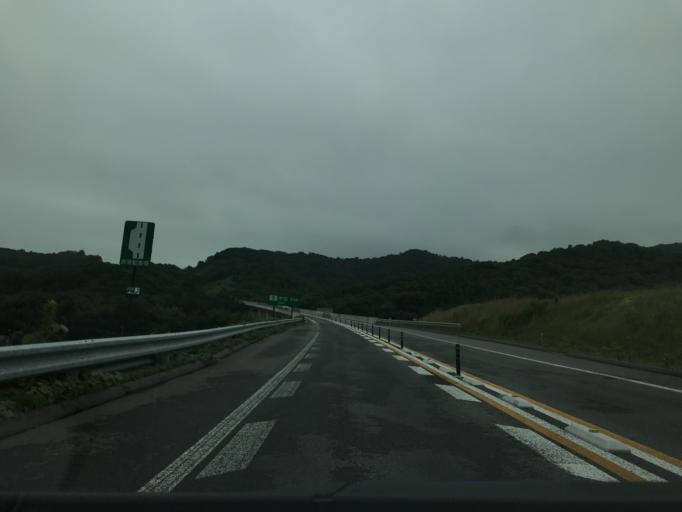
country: JP
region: Fukuoka
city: Nakatsu
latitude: 33.5052
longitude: 131.2969
